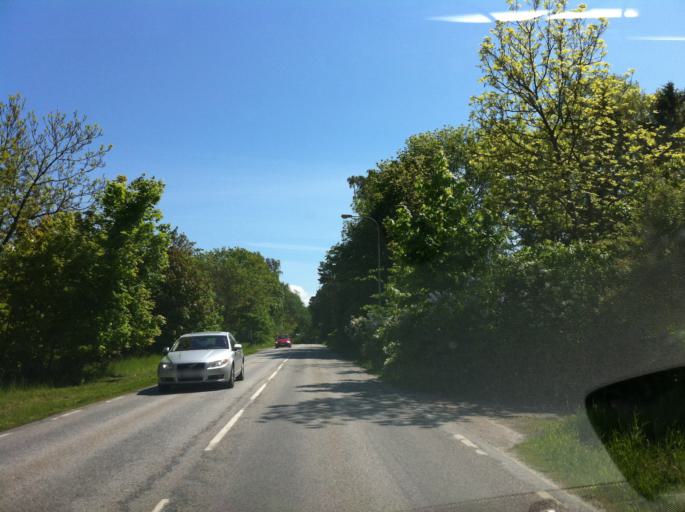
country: SE
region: Skane
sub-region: Kavlinge Kommun
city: Hofterup
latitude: 55.7991
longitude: 12.9892
